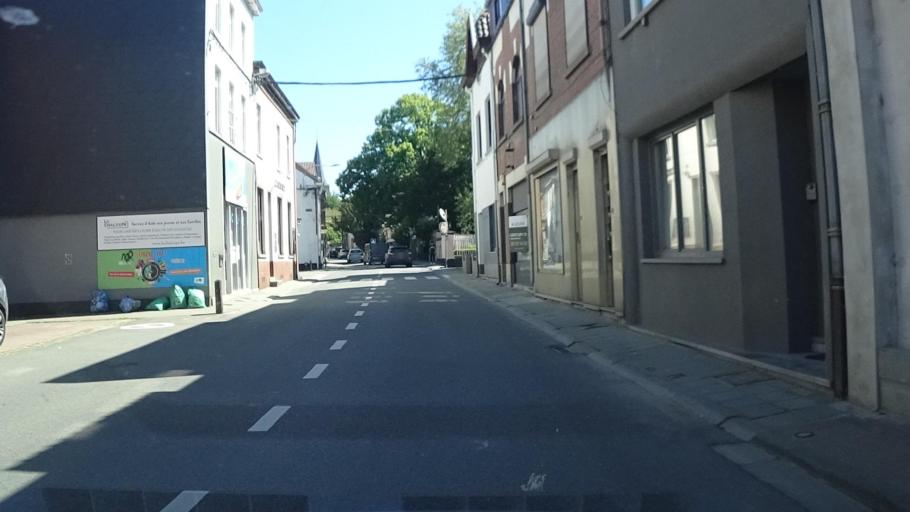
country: BE
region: Wallonia
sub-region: Province du Brabant Wallon
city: Court-Saint-Etienne
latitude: 50.6453
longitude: 4.5668
